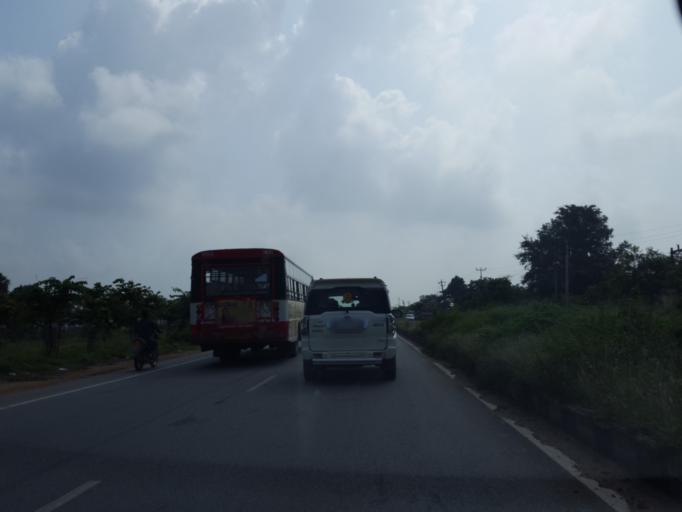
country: IN
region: Telangana
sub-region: Rangareddi
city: Ghatkesar
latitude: 17.2944
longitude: 78.7433
